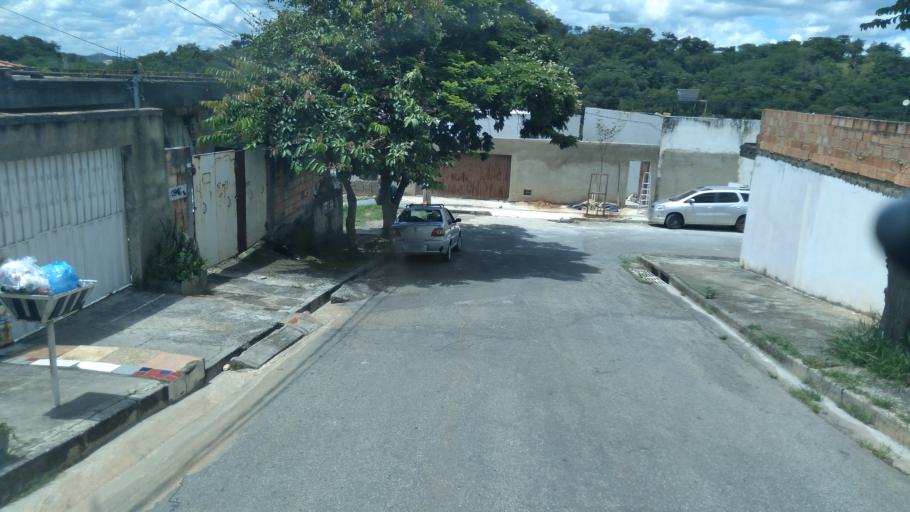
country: BR
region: Minas Gerais
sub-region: Santa Luzia
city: Santa Luzia
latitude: -19.8563
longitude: -43.8743
